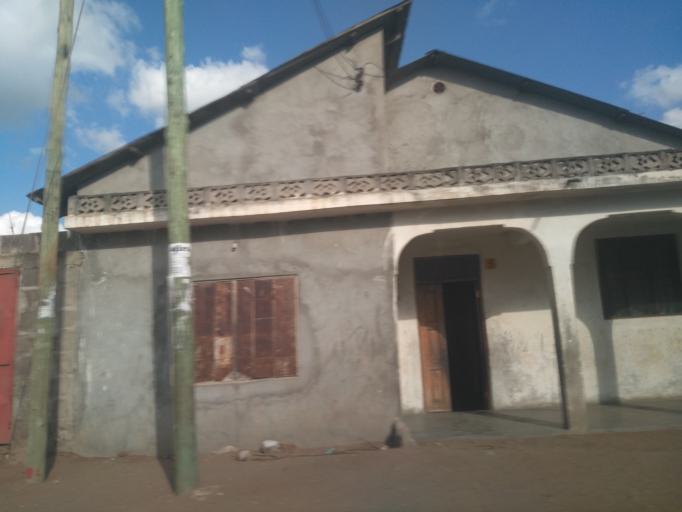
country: TZ
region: Dar es Salaam
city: Dar es Salaam
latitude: -6.8640
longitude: 39.2599
